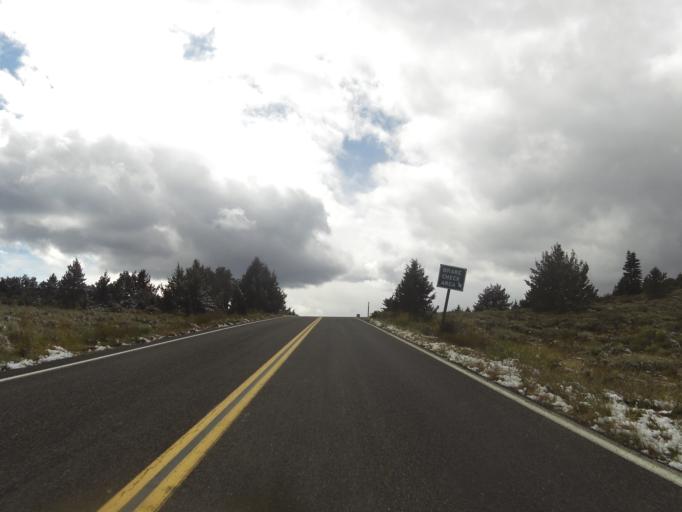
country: US
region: Nevada
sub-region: Douglas County
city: Gardnerville Ranchos
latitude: 38.6694
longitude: -119.6295
